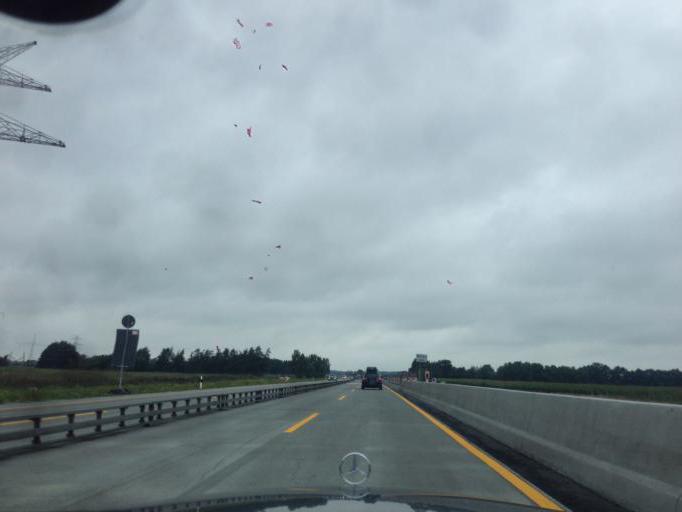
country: DE
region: Schleswig-Holstein
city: Bimohlen
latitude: 53.9577
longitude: 9.9503
